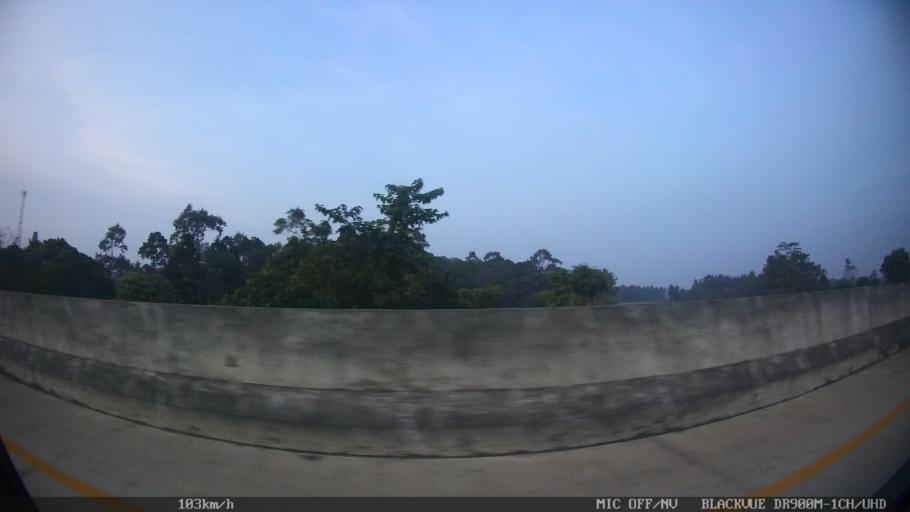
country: ID
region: Lampung
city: Pasuruan
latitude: -5.7115
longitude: 105.6489
